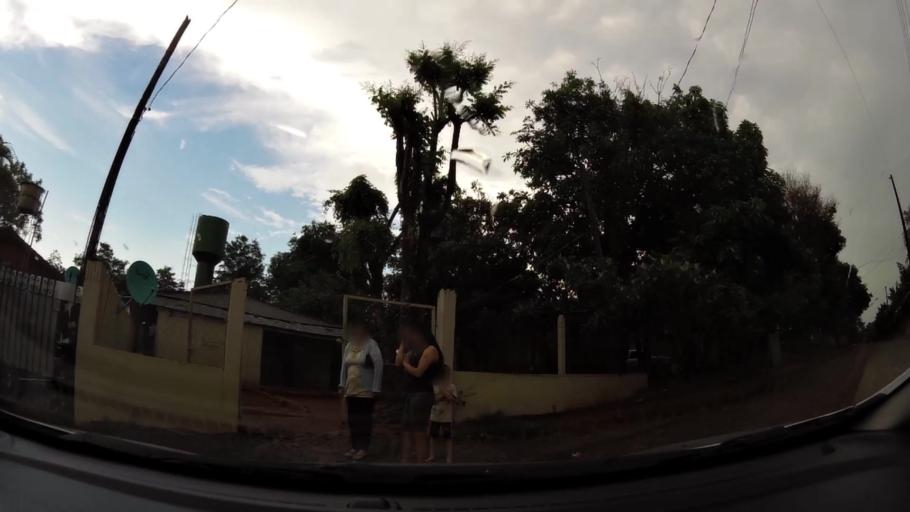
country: PY
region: Alto Parana
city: Presidente Franco
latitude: -25.5403
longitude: -54.6553
